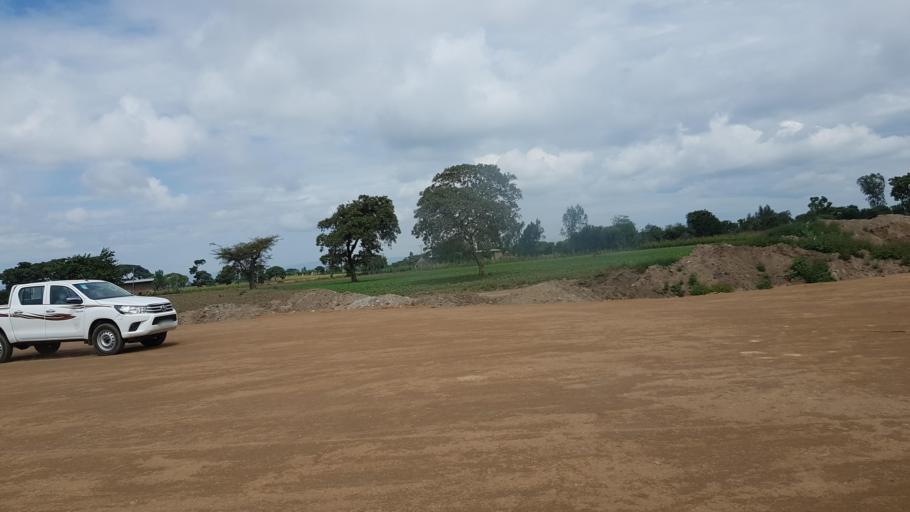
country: ET
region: Oromiya
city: Shashemene
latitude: 7.2577
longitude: 38.5947
